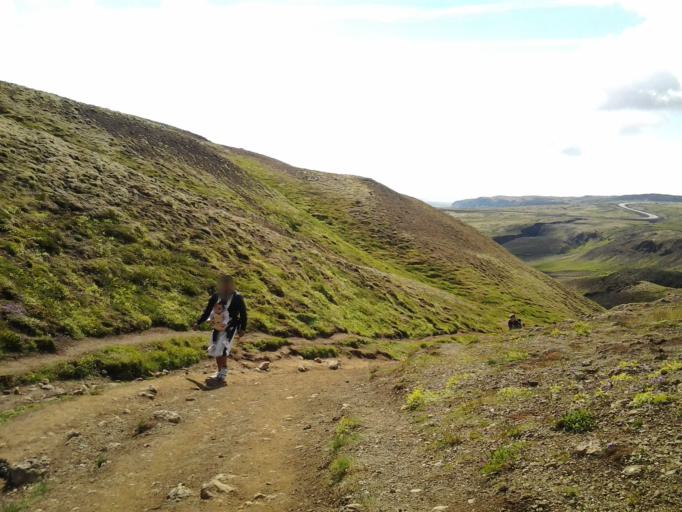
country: IS
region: South
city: Hveragerdi
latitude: 64.0317
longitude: -21.2139
